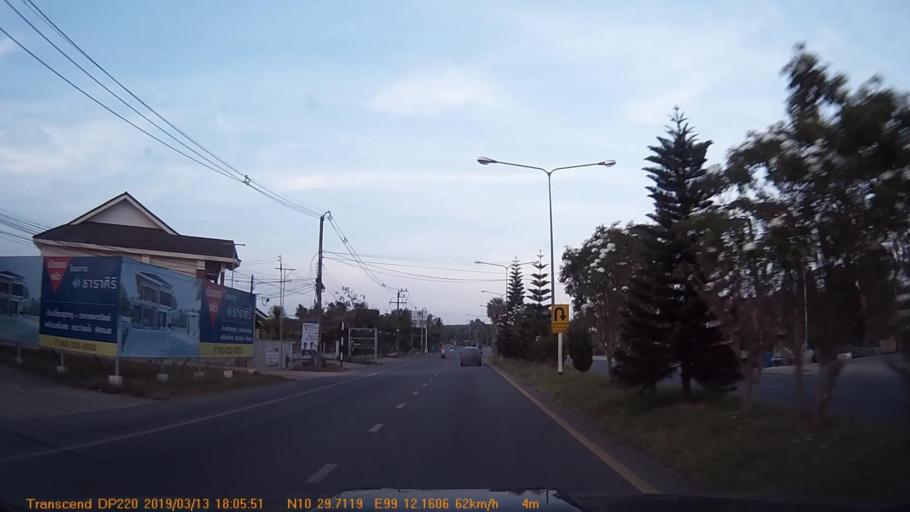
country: TH
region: Chumphon
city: Chumphon
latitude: 10.4955
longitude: 99.2029
